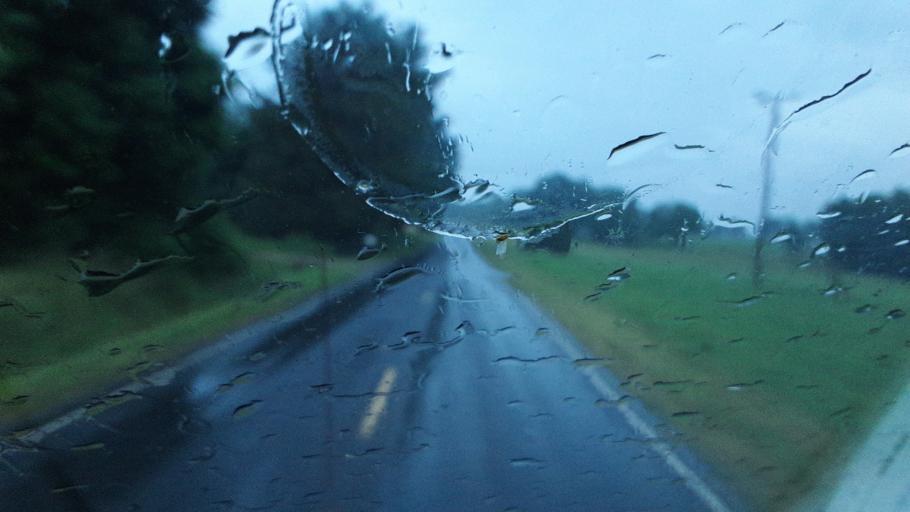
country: US
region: North Carolina
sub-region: Yadkin County
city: Jonesville
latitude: 36.0718
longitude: -80.8378
